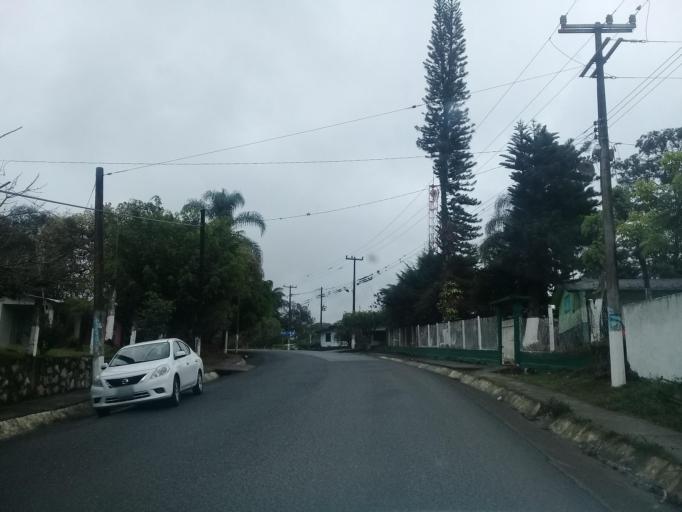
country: MX
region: Veracruz
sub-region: Amatlan de los Reyes
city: Trapiche Viejo
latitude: 18.8252
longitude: -96.9573
